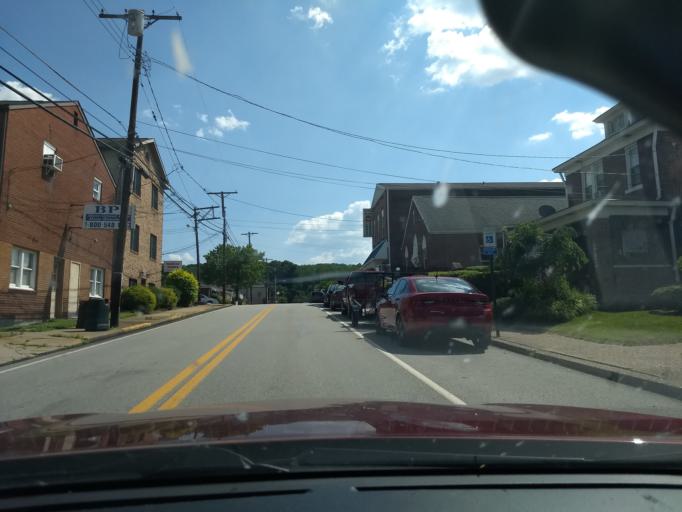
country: US
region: Pennsylvania
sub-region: Westmoreland County
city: Trafford
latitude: 40.3840
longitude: -79.7617
